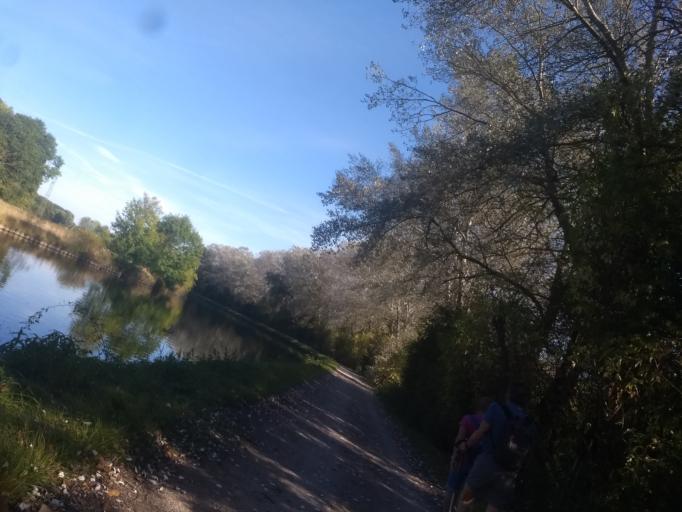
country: FR
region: Nord-Pas-de-Calais
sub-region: Departement du Pas-de-Calais
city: Roeux
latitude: 50.2913
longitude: 2.8891
